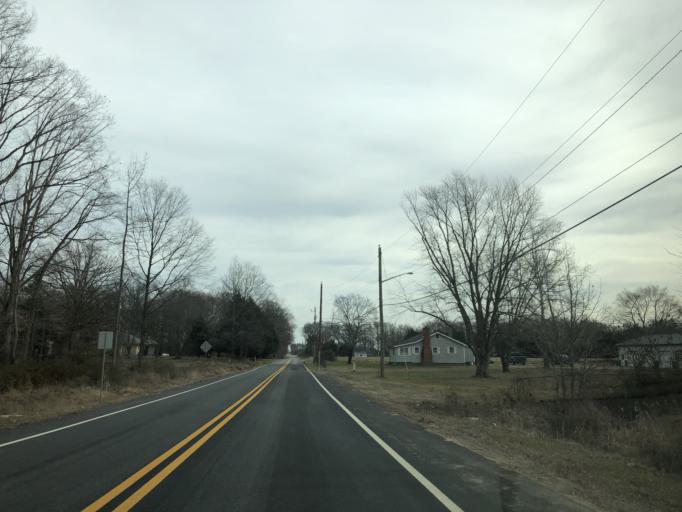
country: US
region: Delaware
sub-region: New Castle County
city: Middletown
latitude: 39.4146
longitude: -75.7646
